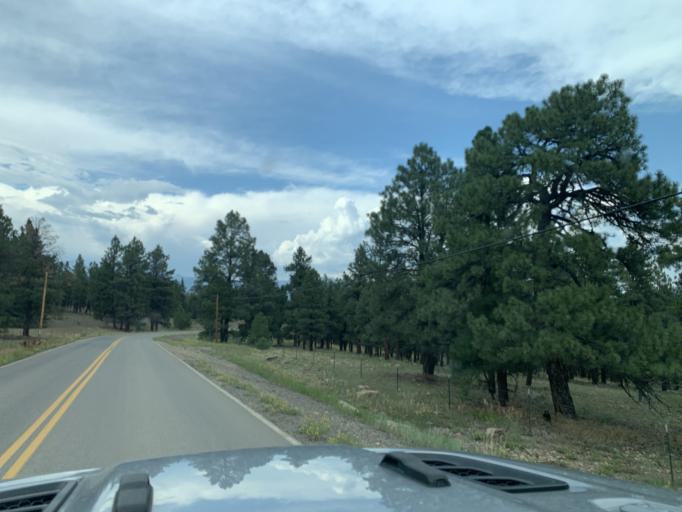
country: US
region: Colorado
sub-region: Archuleta County
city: Pagosa Springs
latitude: 37.2464
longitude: -107.0258
